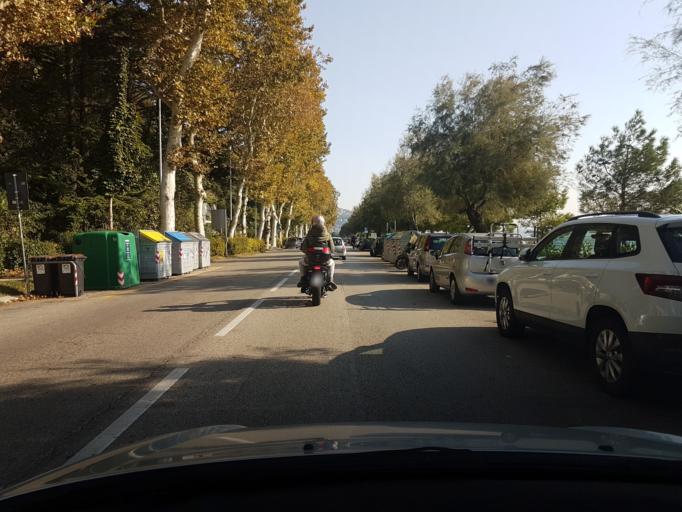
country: IT
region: Friuli Venezia Giulia
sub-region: Provincia di Trieste
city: Prosecco-Contovello
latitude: 45.6924
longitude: 13.7390
